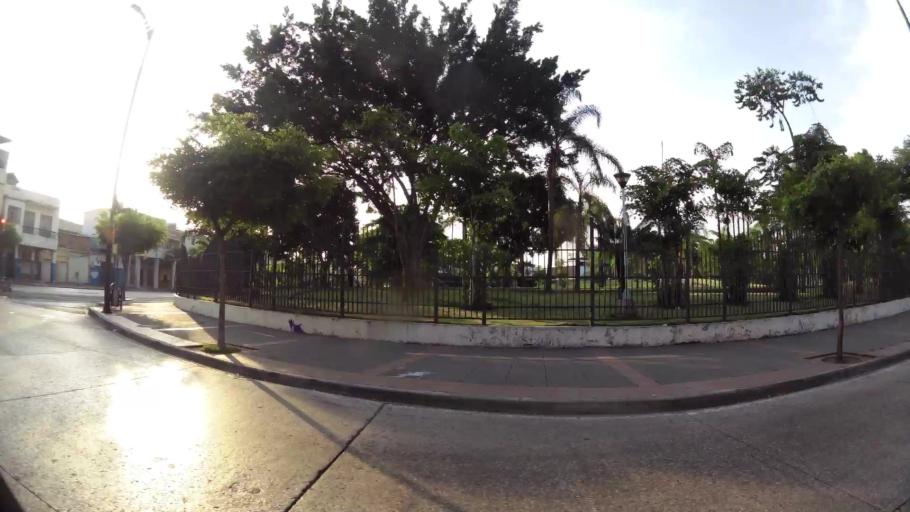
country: EC
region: Guayas
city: Guayaquil
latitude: -2.2086
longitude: -79.8951
